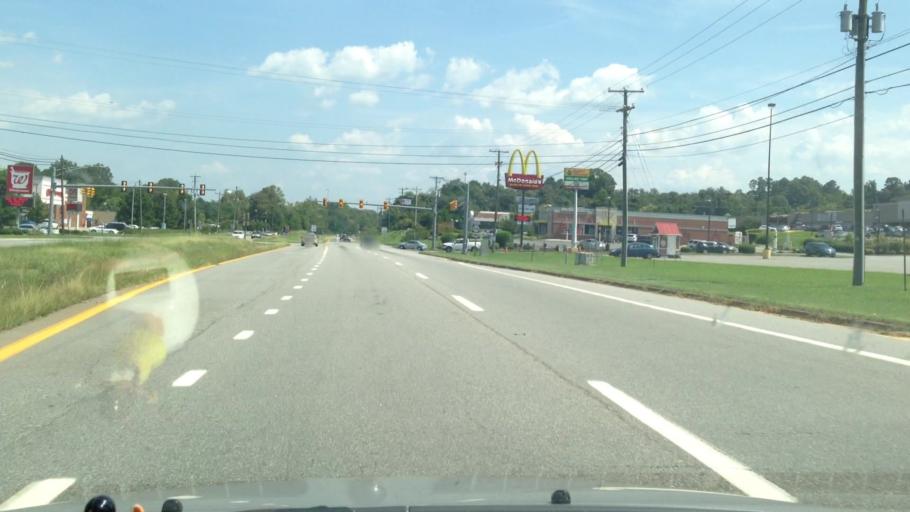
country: US
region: Virginia
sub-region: City of Martinsville
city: Martinsville
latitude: 36.6539
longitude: -79.8756
